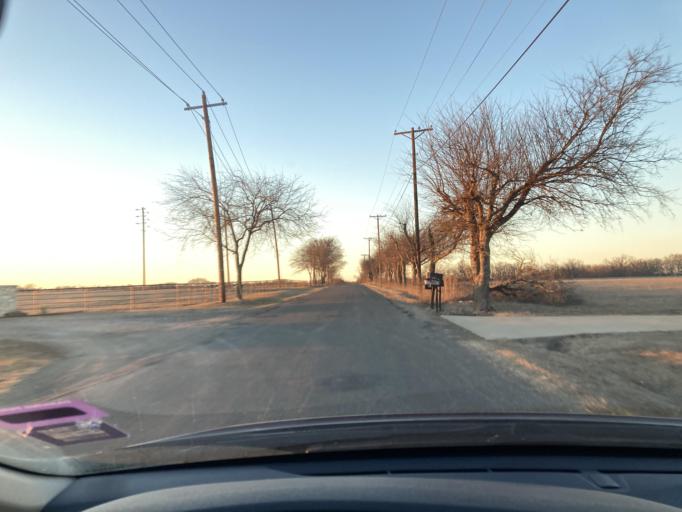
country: US
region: Texas
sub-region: Ellis County
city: Nash
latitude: 32.2868
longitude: -96.9074
